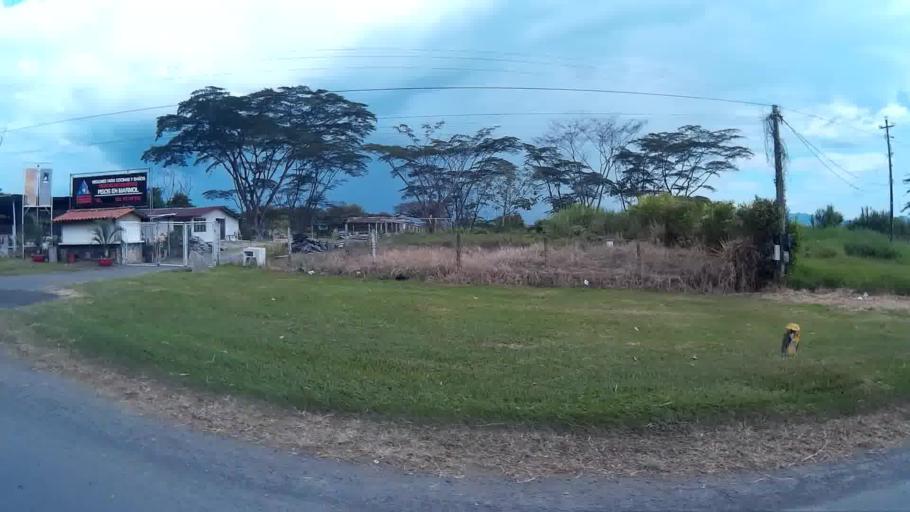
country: CO
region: Valle del Cauca
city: Cartago
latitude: 4.8064
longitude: -75.8165
